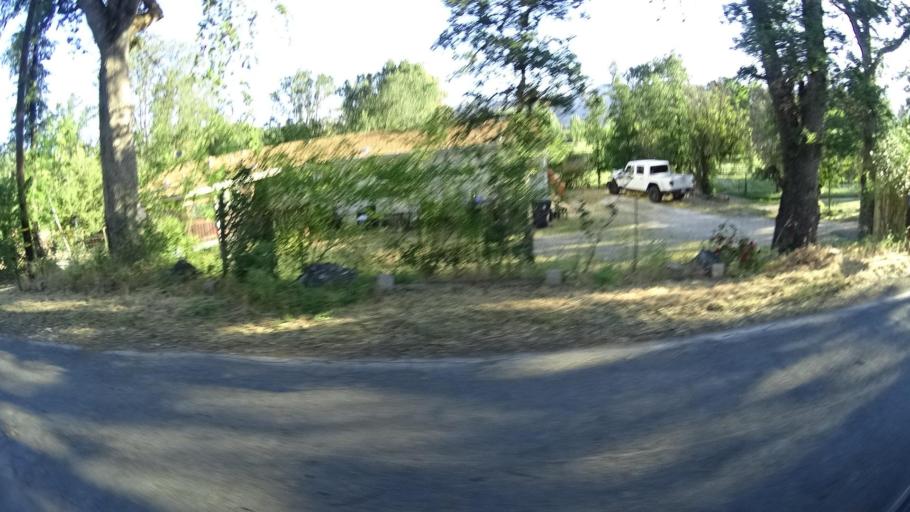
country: US
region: California
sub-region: Lake County
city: Upper Lake
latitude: 39.1676
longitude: -122.9026
